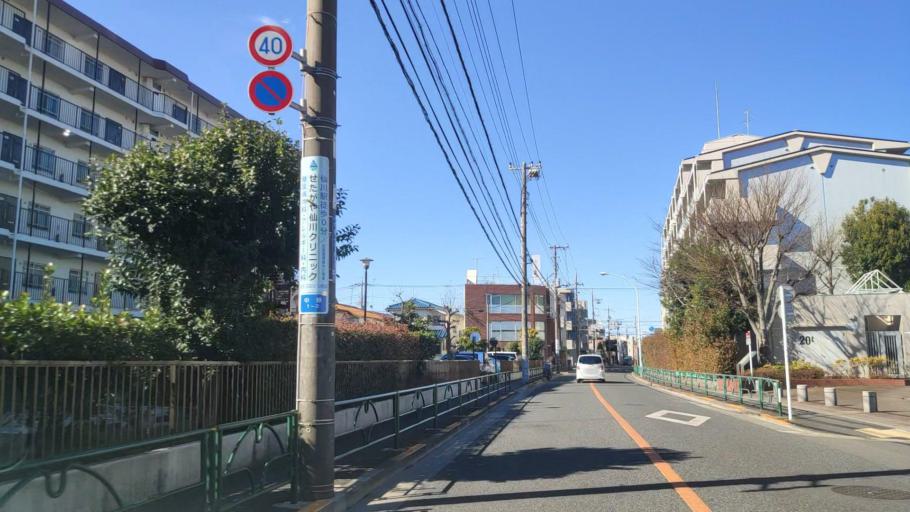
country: JP
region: Tokyo
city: Mitaka-shi
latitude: 35.6657
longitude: 139.5798
